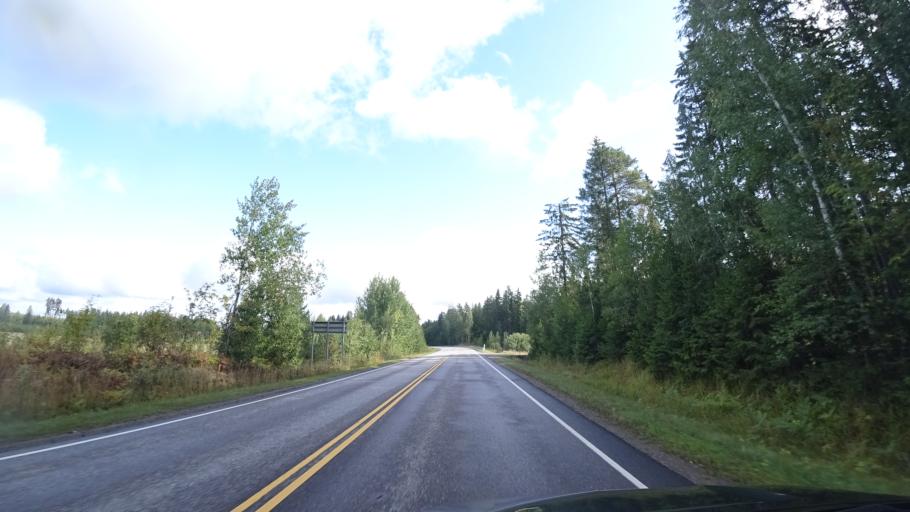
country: FI
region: Uusimaa
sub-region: Helsinki
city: Hyvinge
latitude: 60.5347
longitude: 24.9209
